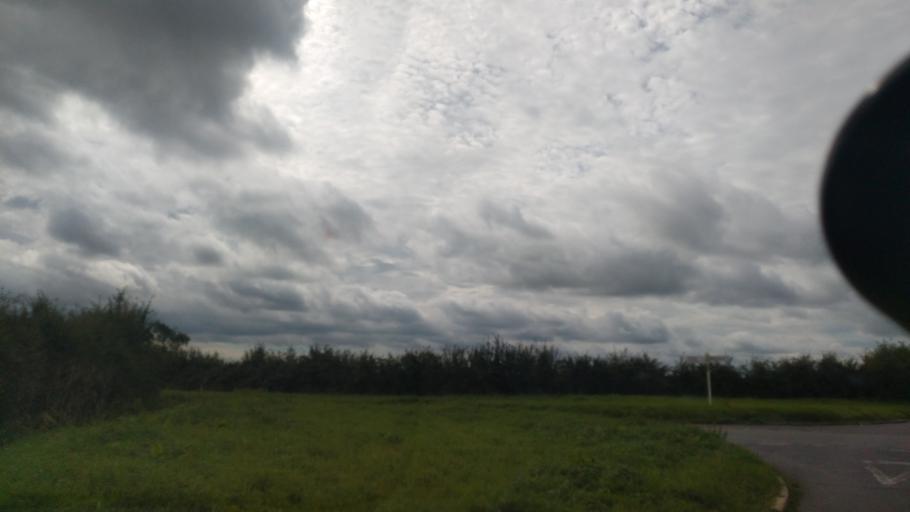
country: GB
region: England
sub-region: Wiltshire
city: Corsham
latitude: 51.4377
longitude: -2.1537
